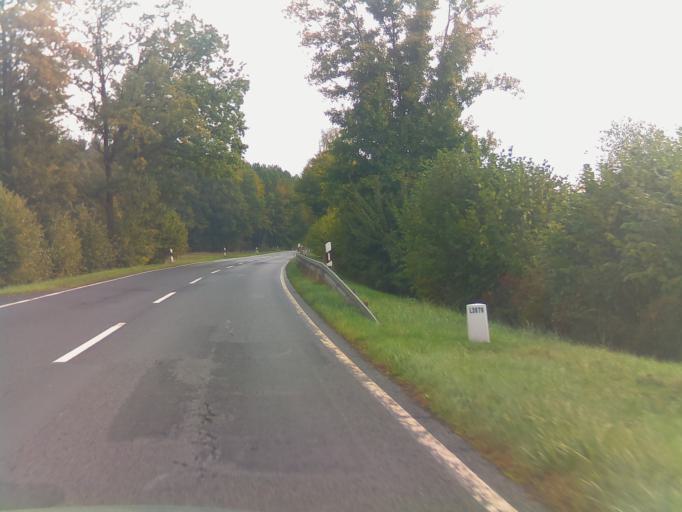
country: DE
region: Hesse
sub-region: Regierungsbezirk Kassel
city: Neuhof
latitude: 50.5142
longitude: 9.5832
